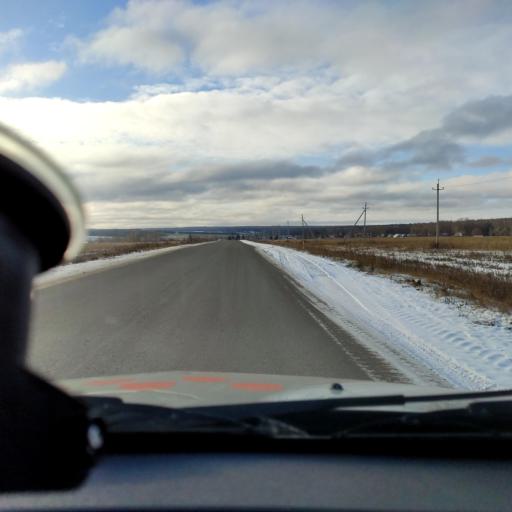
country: RU
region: Bashkortostan
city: Mikhaylovka
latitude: 54.8097
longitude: 55.7839
